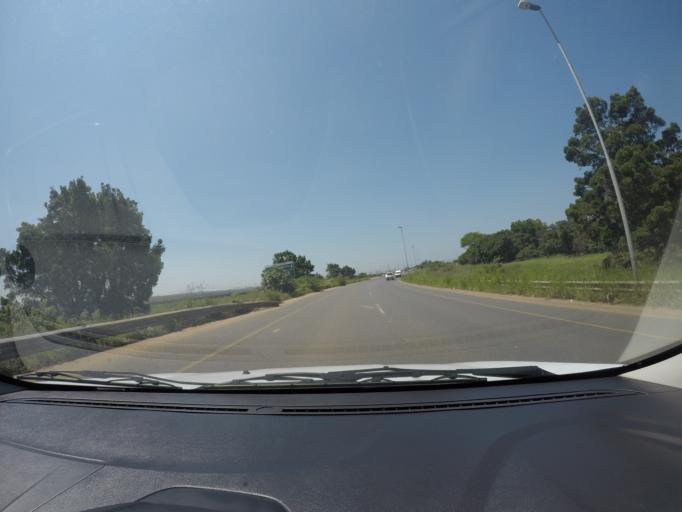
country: ZA
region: KwaZulu-Natal
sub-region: uThungulu District Municipality
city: Empangeni
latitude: -28.7773
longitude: 31.9583
